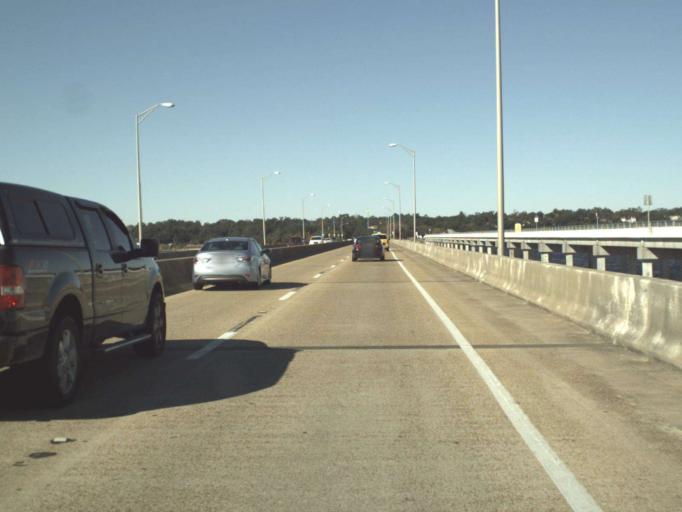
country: US
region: Florida
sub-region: Escambia County
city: East Pensacola Heights
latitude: 30.4108
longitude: -87.1910
